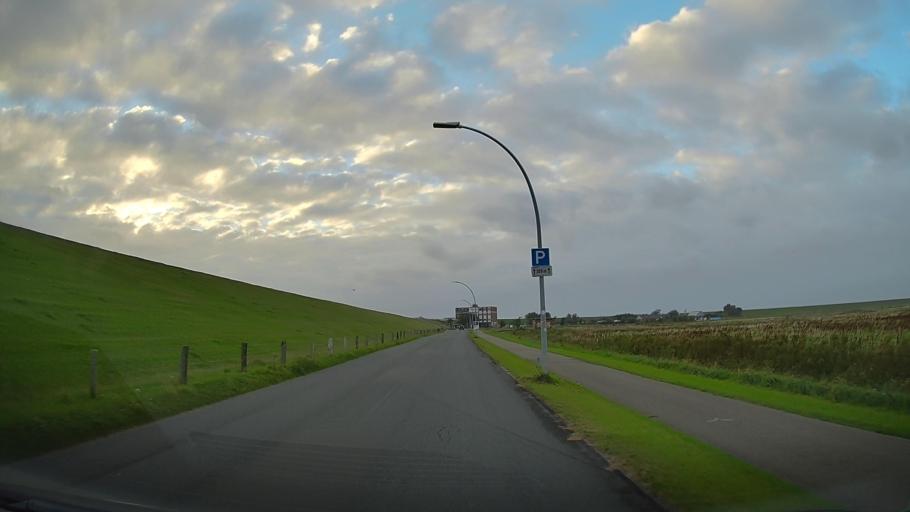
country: DE
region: Schleswig-Holstein
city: Schobull
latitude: 54.4763
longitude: 9.0154
